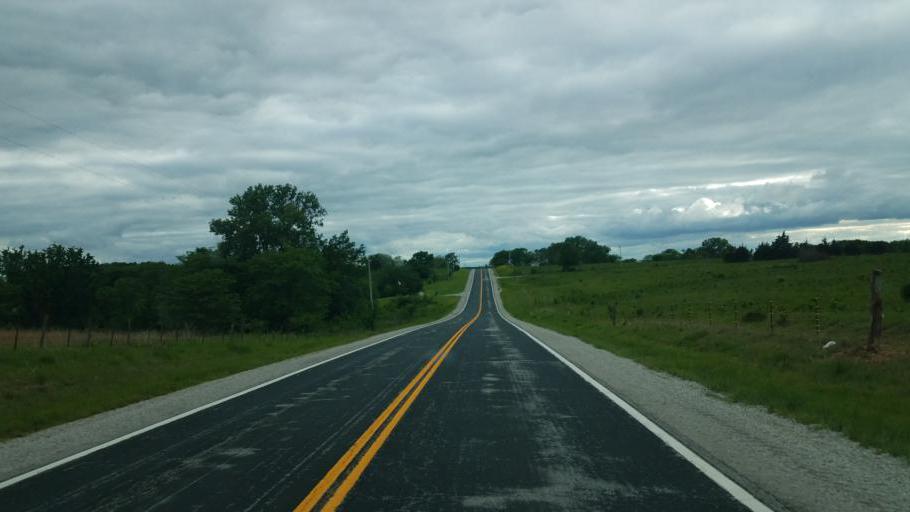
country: US
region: Missouri
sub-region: Mercer County
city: Princeton
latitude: 40.3738
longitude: -93.7149
